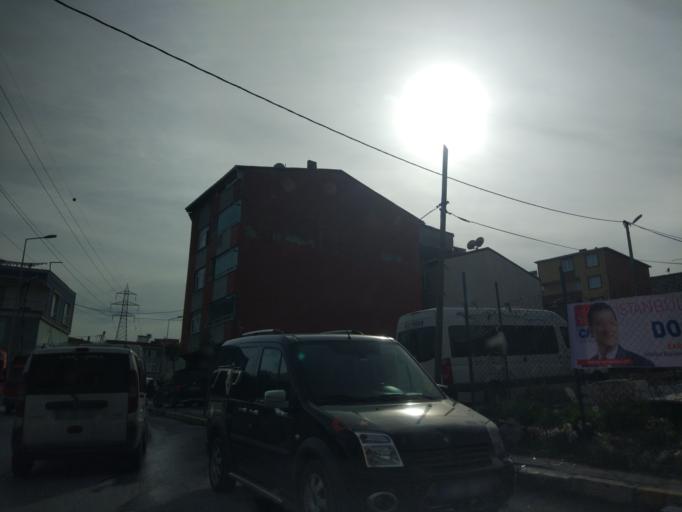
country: TR
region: Istanbul
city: Esenyurt
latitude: 41.0398
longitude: 28.7021
